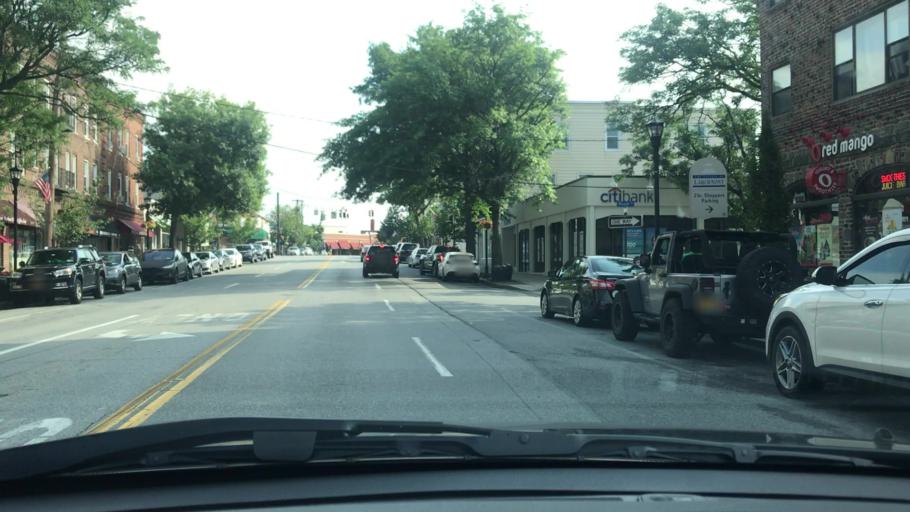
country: US
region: New York
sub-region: Westchester County
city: Larchmont
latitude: 40.9320
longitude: -73.7596
